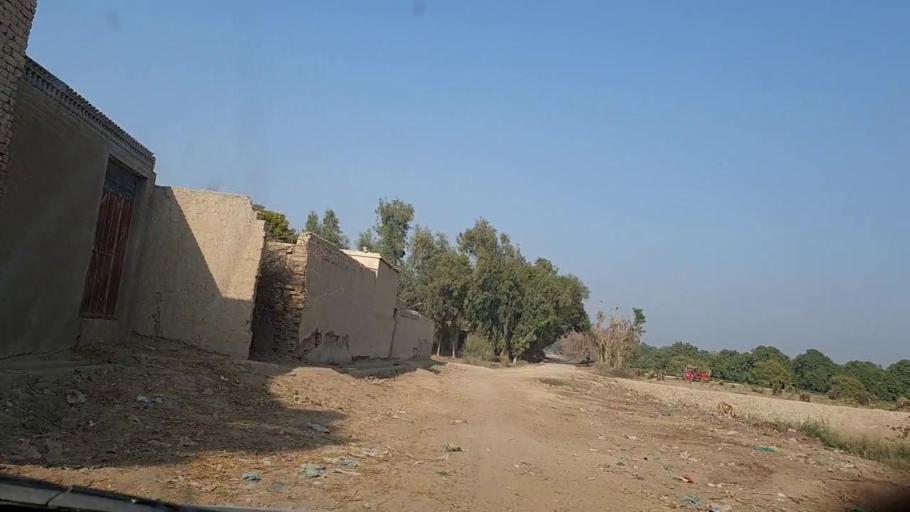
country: PK
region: Sindh
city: Moro
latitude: 26.7945
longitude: 67.9422
